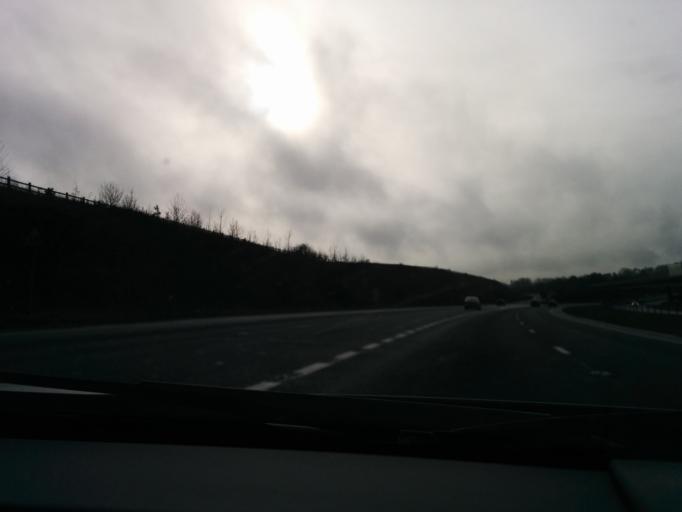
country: GB
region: England
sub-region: West Berkshire
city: Winterbourne
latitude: 51.4371
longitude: -1.3207
